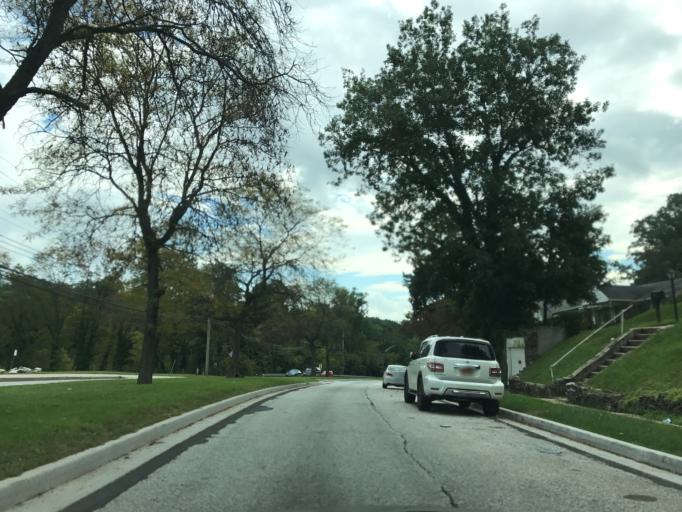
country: US
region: Maryland
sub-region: Baltimore County
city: Woodlawn
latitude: 39.3260
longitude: -76.7170
